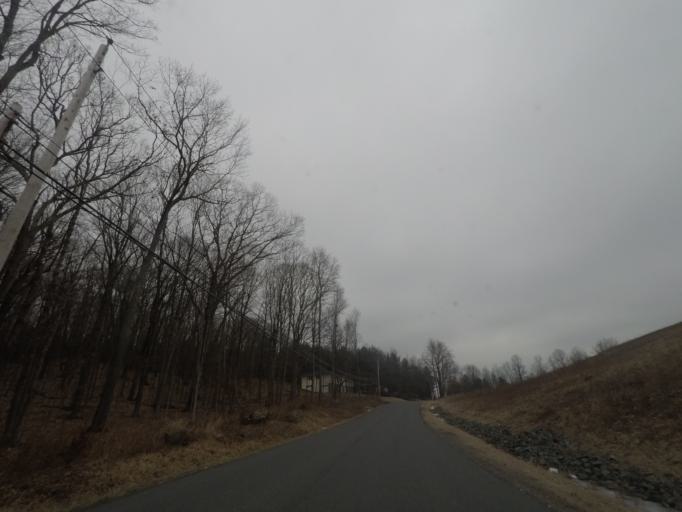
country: US
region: New York
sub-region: Rensselaer County
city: East Greenbush
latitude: 42.5696
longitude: -73.6616
